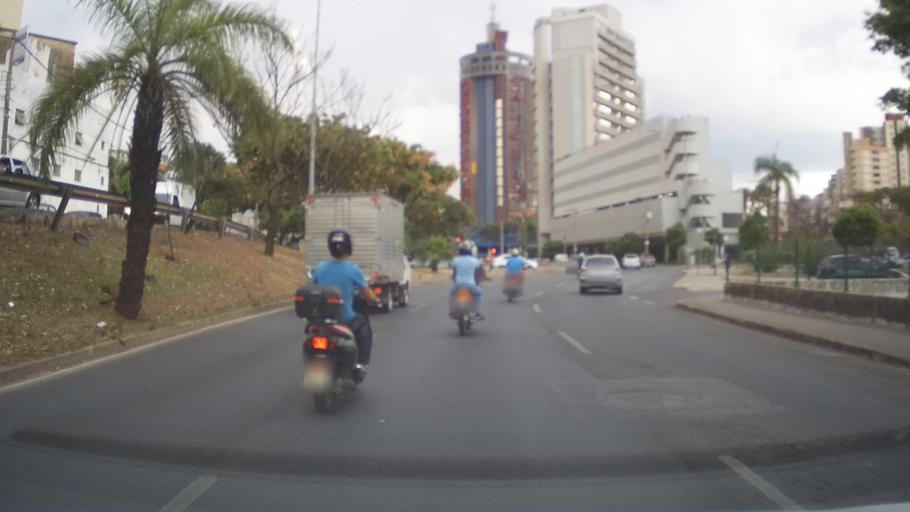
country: BR
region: Minas Gerais
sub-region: Belo Horizonte
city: Belo Horizonte
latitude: -19.9203
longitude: -43.9223
